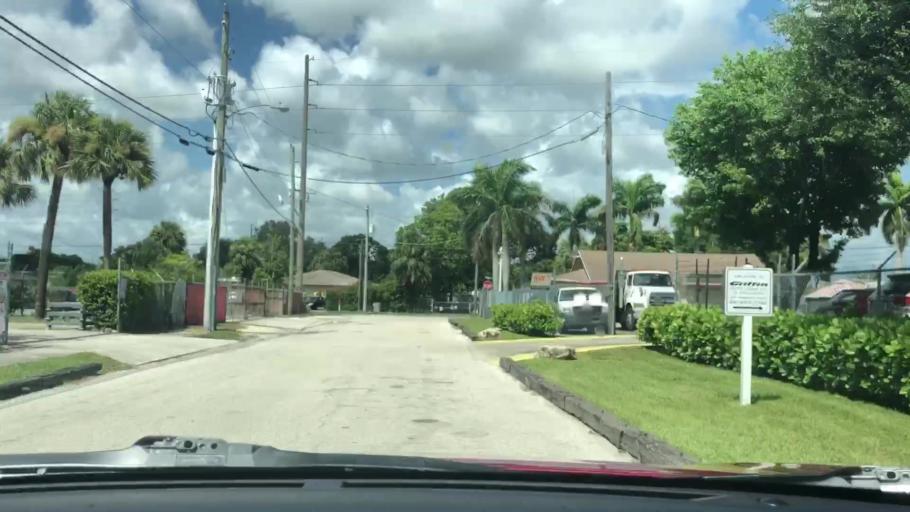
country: US
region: Florida
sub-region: Palm Beach County
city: West Palm Beach
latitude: 26.6990
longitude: -80.0654
